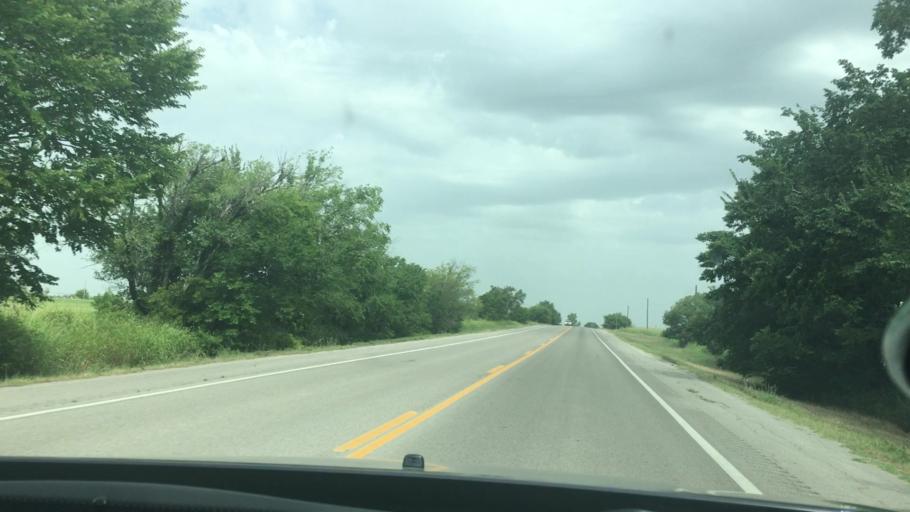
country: US
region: Oklahoma
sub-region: Garvin County
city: Pauls Valley
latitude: 34.8413
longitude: -97.2729
